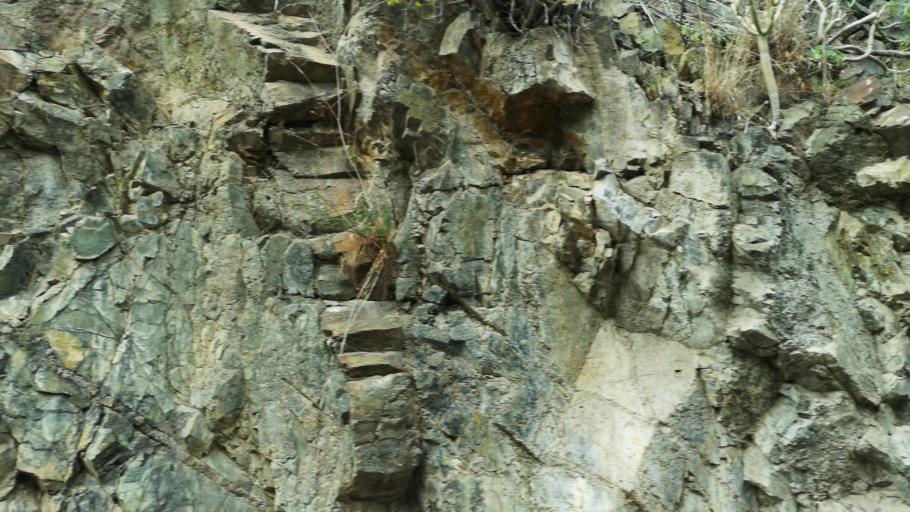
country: ES
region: Canary Islands
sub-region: Provincia de Santa Cruz de Tenerife
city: Vallehermosa
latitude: 28.1970
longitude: -17.2568
